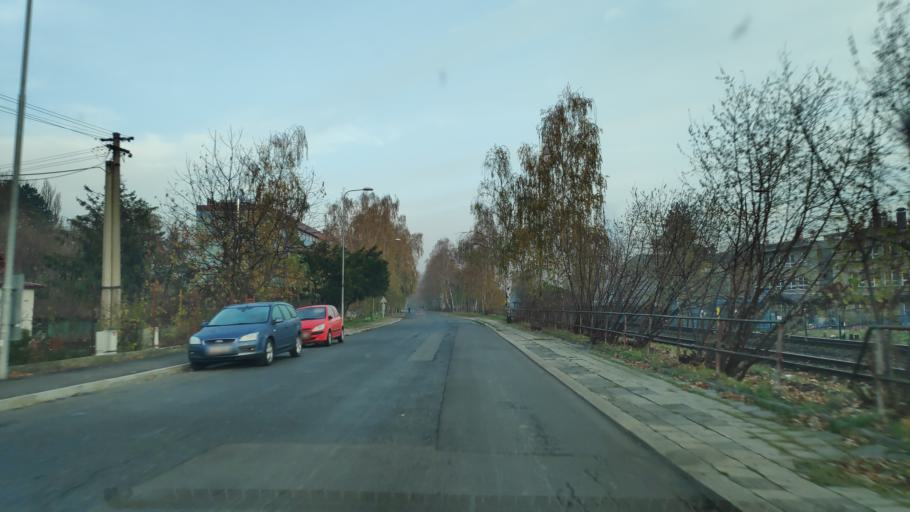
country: CZ
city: Sviadnov
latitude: 49.6928
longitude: 18.3314
